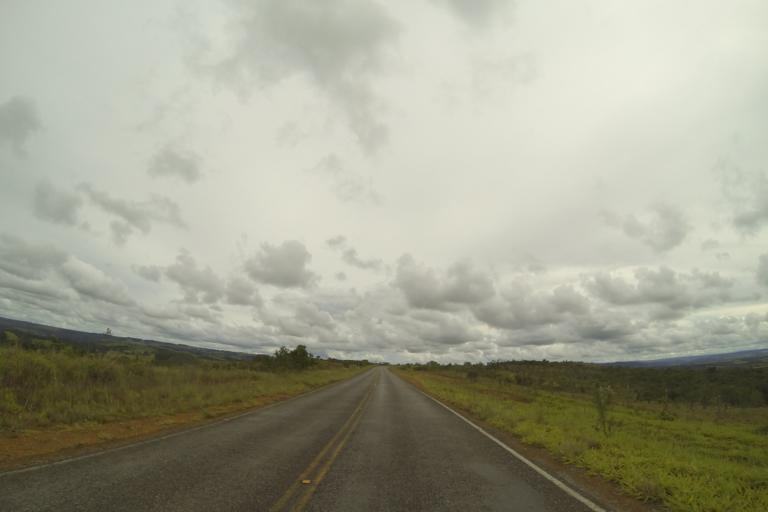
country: BR
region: Minas Gerais
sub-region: Ibia
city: Ibia
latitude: -19.6764
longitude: -46.4414
